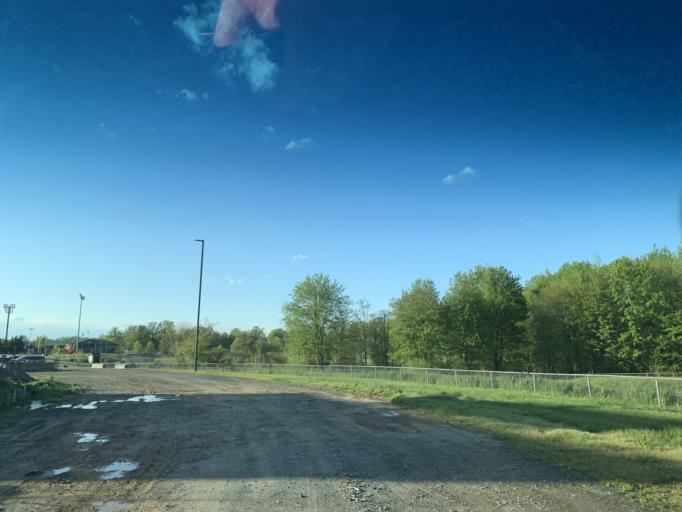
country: US
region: Maryland
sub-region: Harford County
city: Aberdeen
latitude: 39.5308
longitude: -76.1841
